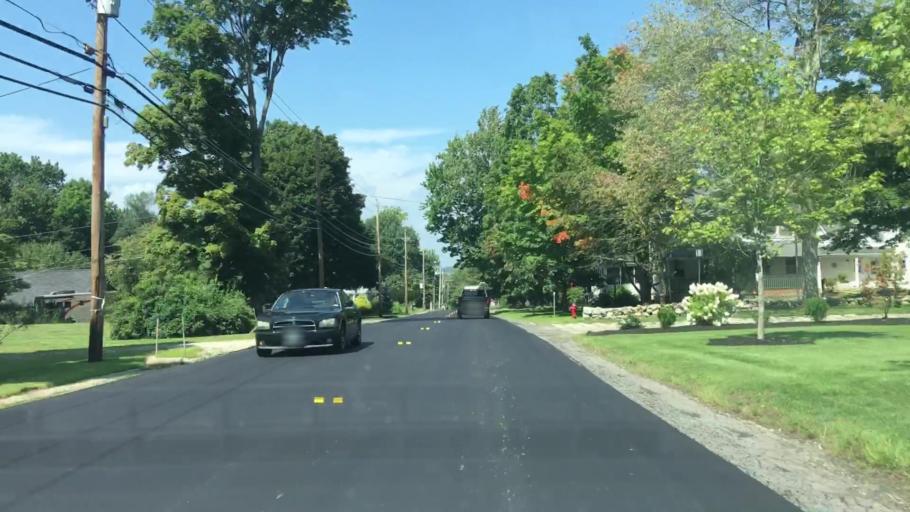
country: US
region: New Hampshire
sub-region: Rockingham County
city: Hampstead
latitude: 42.8799
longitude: -71.1853
